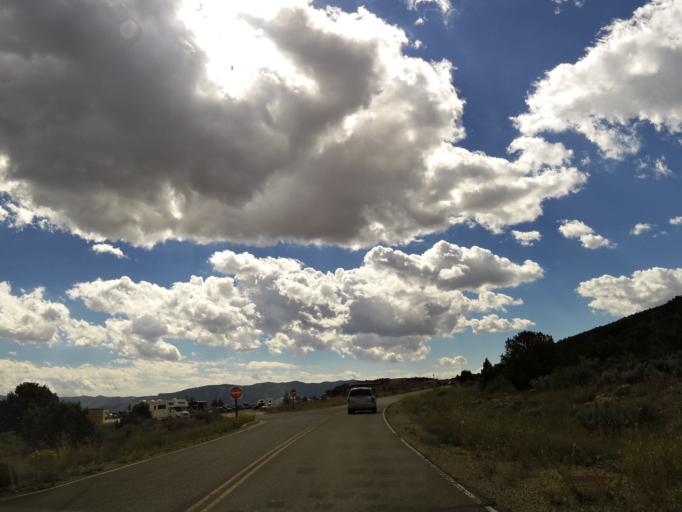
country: US
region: Colorado
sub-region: Montezuma County
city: Mancos
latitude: 37.3380
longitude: -108.4098
